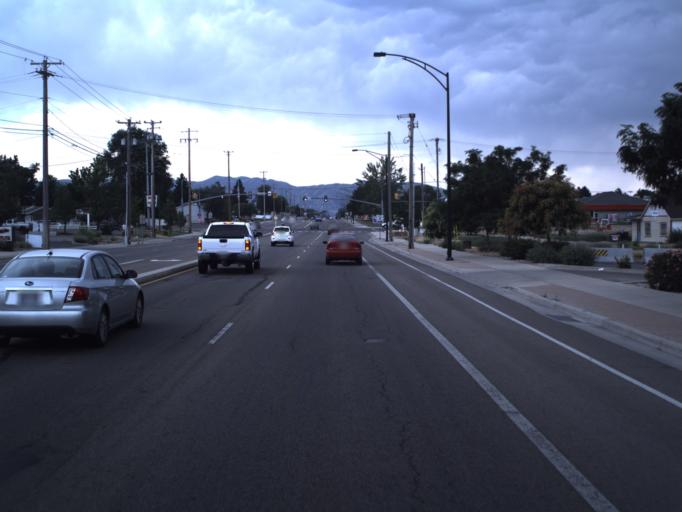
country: US
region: Utah
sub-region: Salt Lake County
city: White City
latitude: 40.5749
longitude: -111.8723
